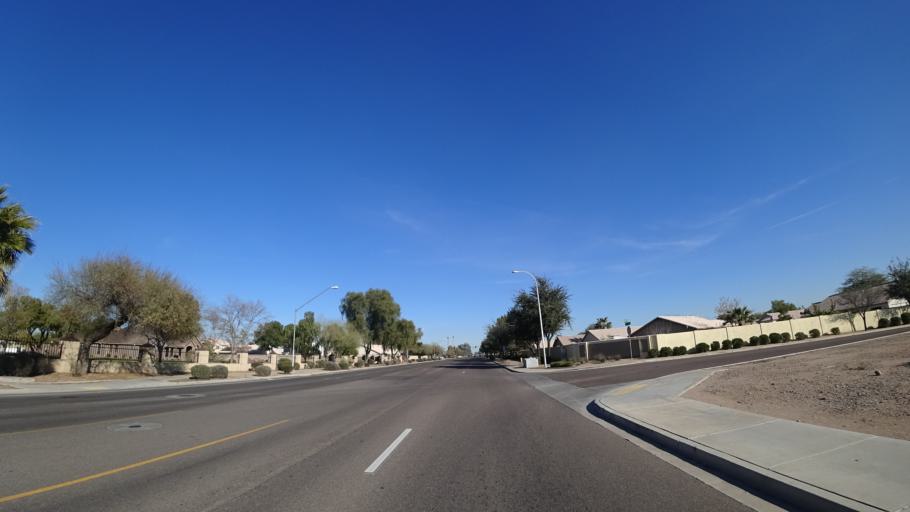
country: US
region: Arizona
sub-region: Maricopa County
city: Glendale
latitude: 33.5233
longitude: -112.2293
